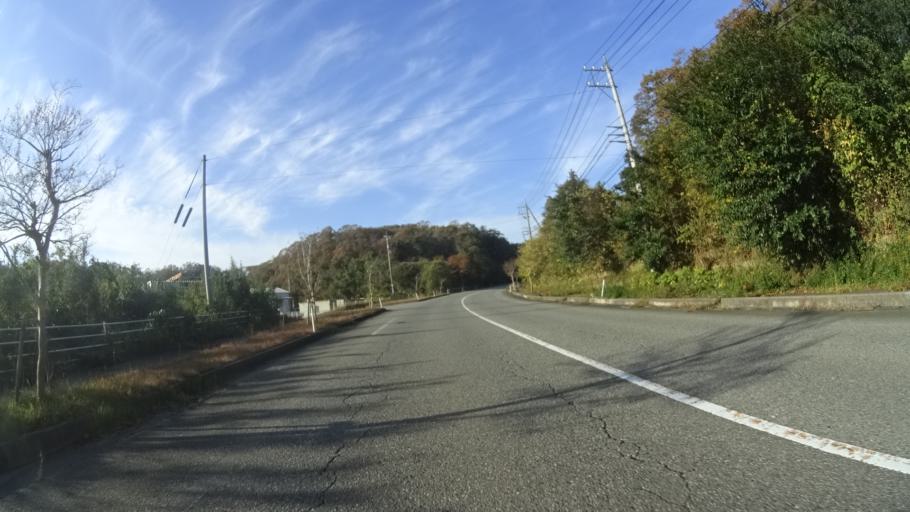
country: JP
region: Ishikawa
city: Hakui
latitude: 37.0335
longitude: 136.7793
